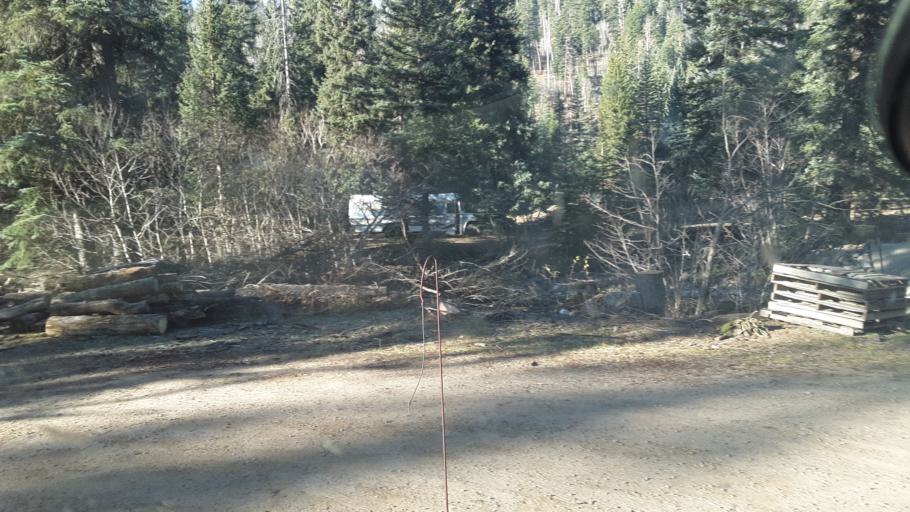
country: US
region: Colorado
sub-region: La Plata County
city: Bayfield
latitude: 37.4274
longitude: -107.6747
